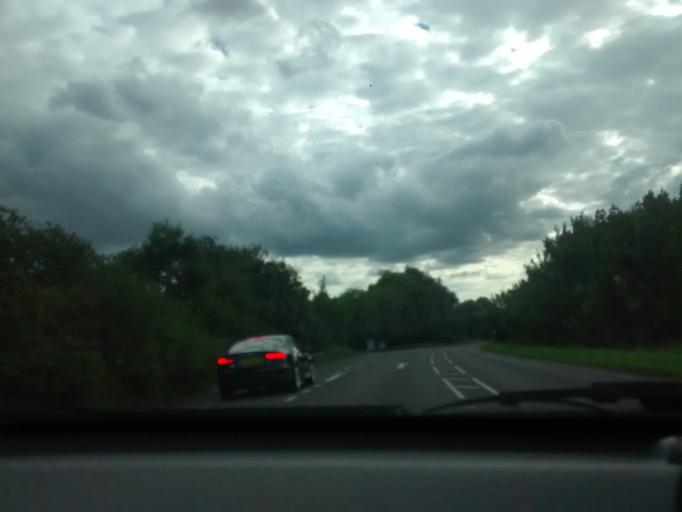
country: GB
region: England
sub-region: Norfolk
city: Downham Market
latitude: 52.5639
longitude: 0.3897
